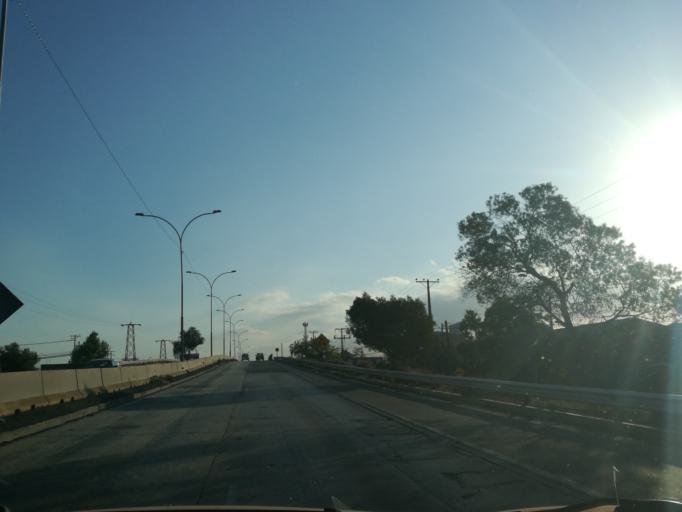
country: CL
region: O'Higgins
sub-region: Provincia de Cachapoal
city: Rancagua
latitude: -34.1779
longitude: -70.7317
